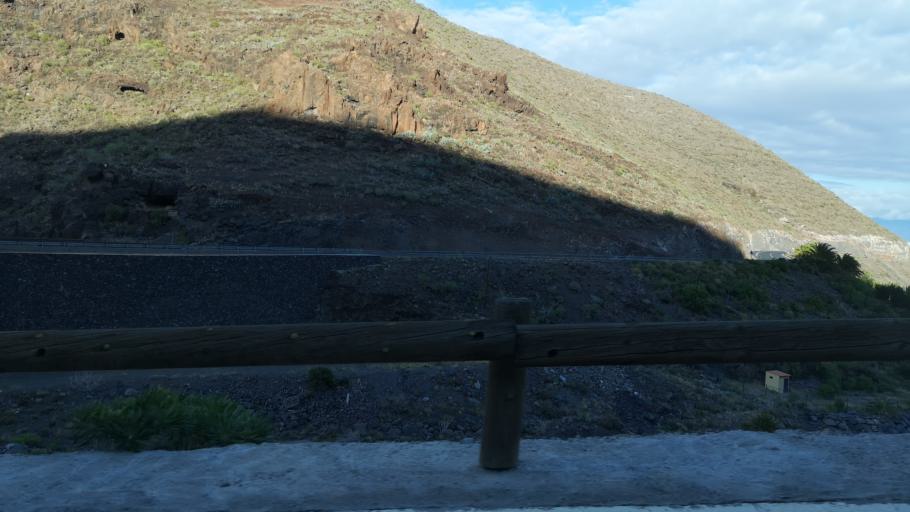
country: ES
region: Canary Islands
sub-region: Provincia de Santa Cruz de Tenerife
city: San Sebastian de la Gomera
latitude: 28.0863
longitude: -17.1303
